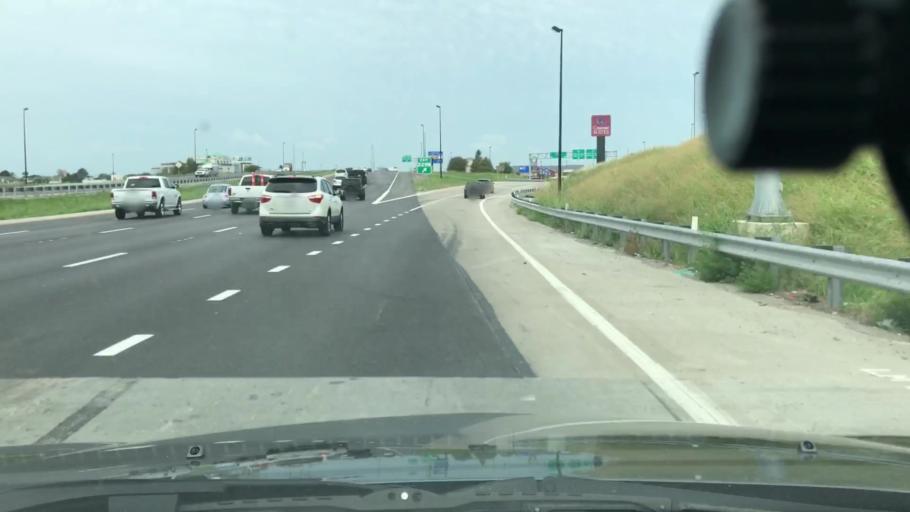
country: US
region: Missouri
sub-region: Saint Charles County
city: Saint Charles
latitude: 38.7675
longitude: -90.4907
